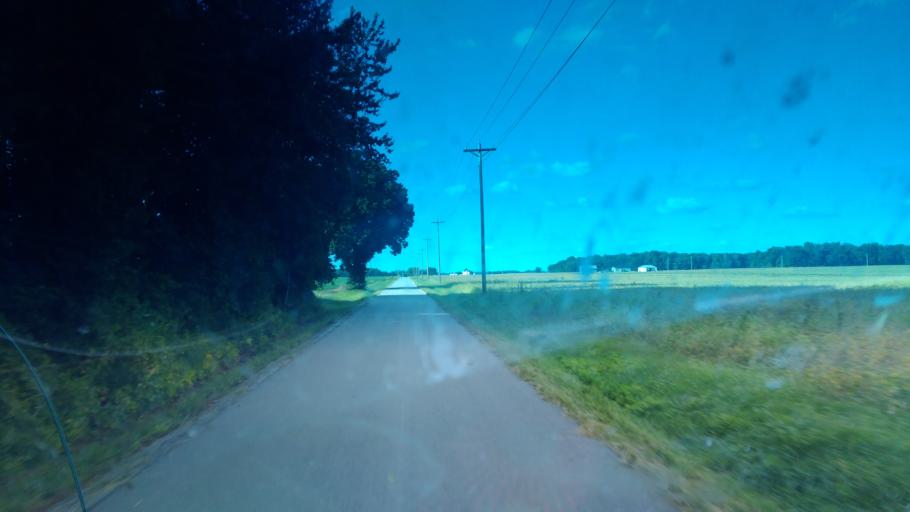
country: US
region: Ohio
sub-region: Hancock County
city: Arlington
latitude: 40.9316
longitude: -83.7657
